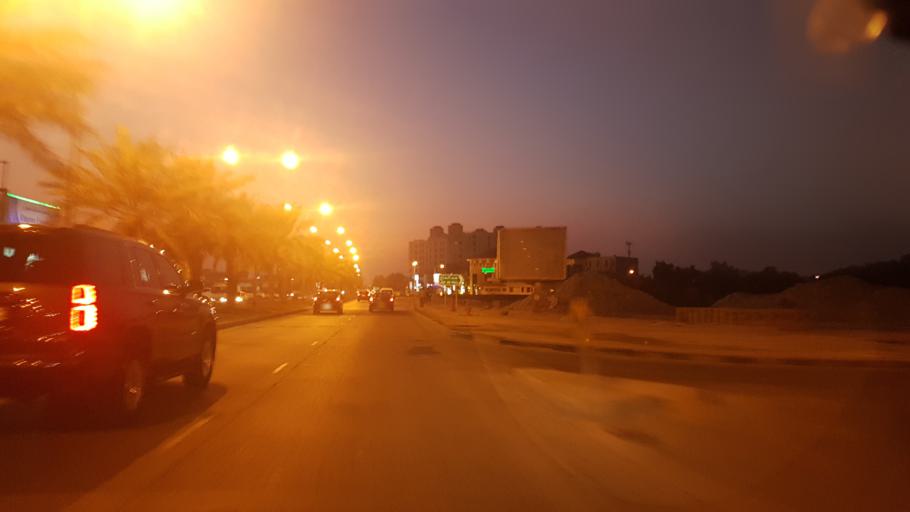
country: BH
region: Manama
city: Jidd Hafs
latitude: 26.2205
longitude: 50.5073
